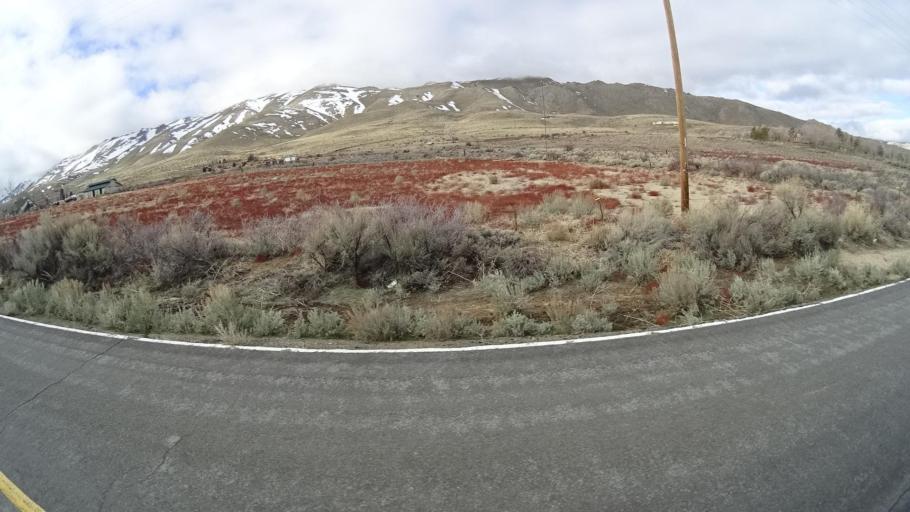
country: US
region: Nevada
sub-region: Washoe County
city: Cold Springs
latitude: 39.8790
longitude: -119.9664
